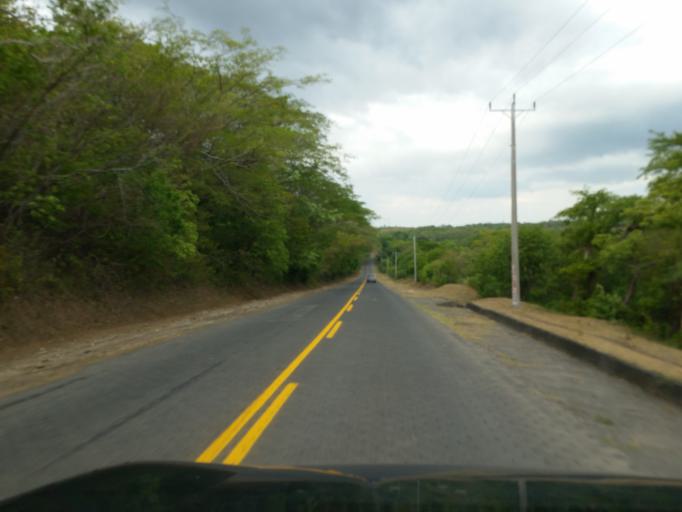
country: NI
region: Managua
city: San Rafael del Sur
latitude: 11.8826
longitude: -86.5147
